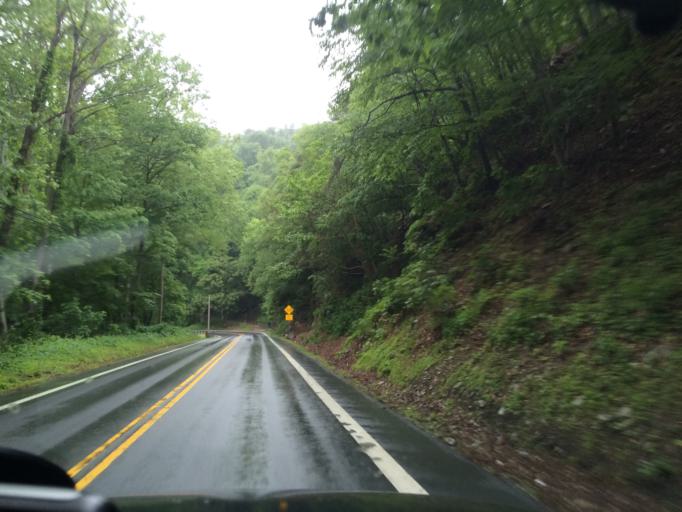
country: US
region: Maryland
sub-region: Frederick County
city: Thurmont
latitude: 39.6502
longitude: -77.4214
